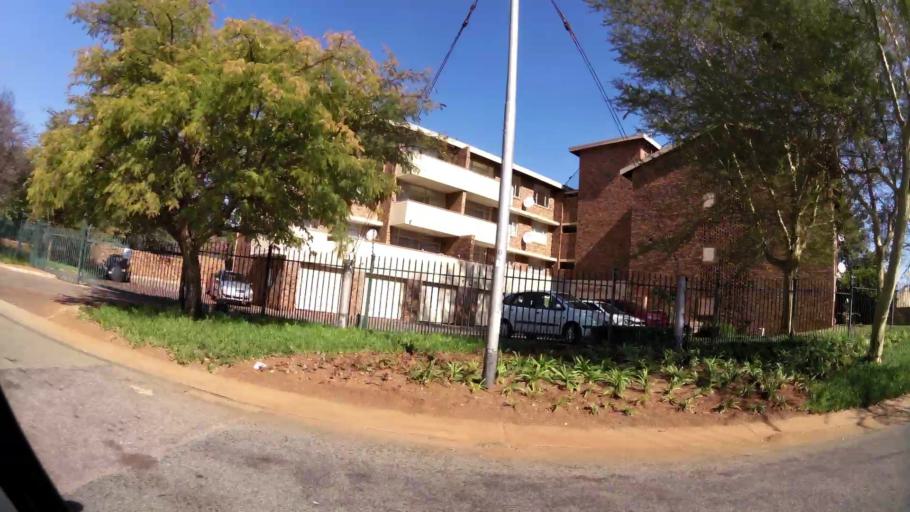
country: ZA
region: Gauteng
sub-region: City of Tshwane Metropolitan Municipality
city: Pretoria
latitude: -25.8013
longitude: 28.2294
